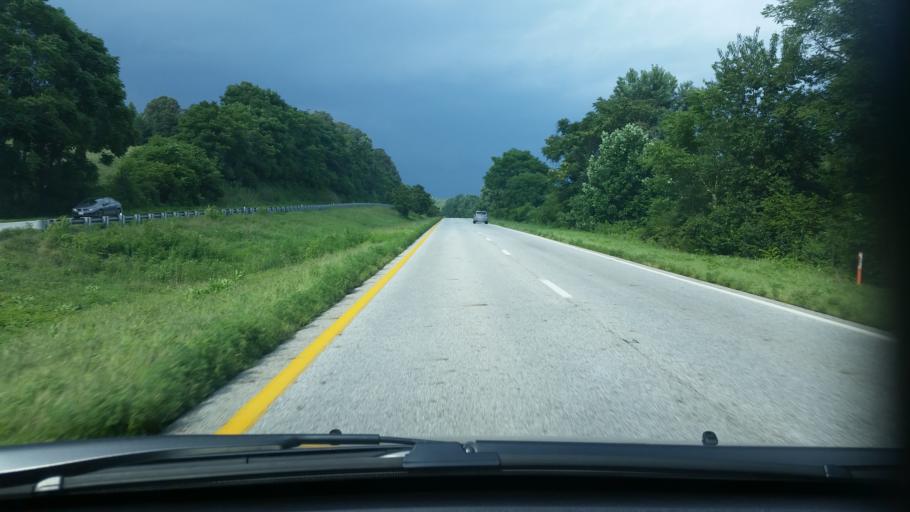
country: US
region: Virginia
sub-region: Nelson County
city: Lovingston
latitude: 37.8162
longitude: -78.8490
